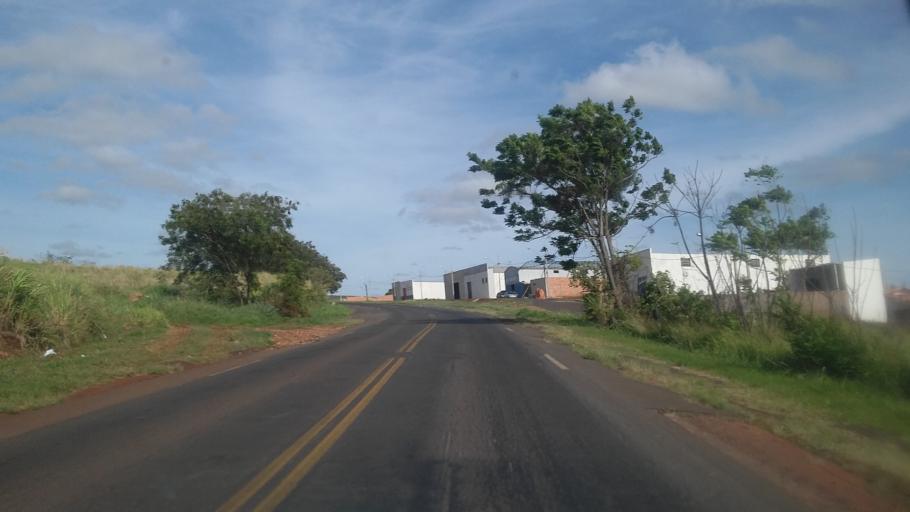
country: BR
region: Parana
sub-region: Santo Antonio Da Platina
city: Santo Antonio da Platina
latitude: -23.2776
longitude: -50.0630
